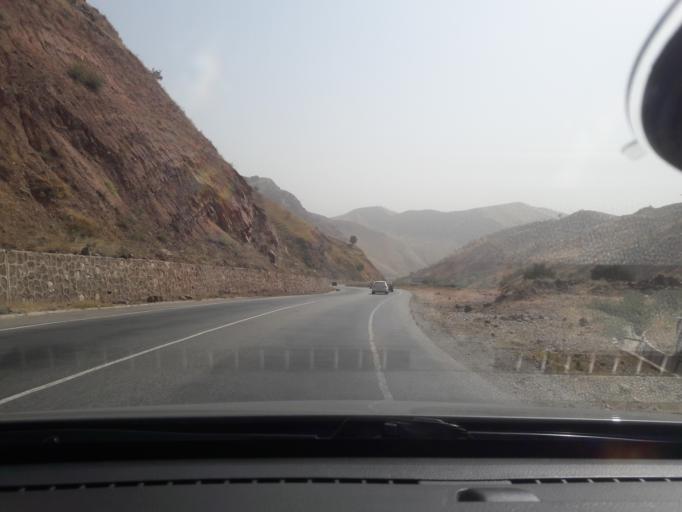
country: TJ
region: Khatlon
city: Norak
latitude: 38.4307
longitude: 69.2235
